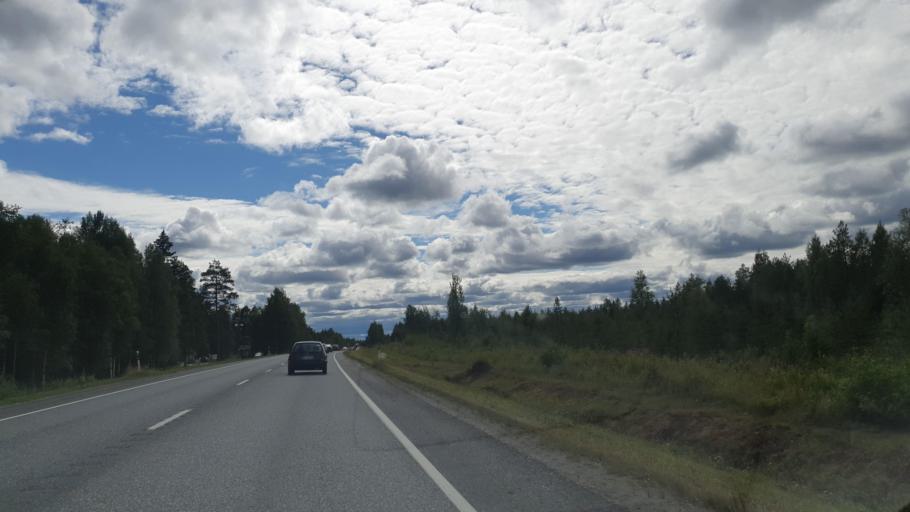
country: FI
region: Kainuu
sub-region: Kajaani
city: Kajaani
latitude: 64.1606
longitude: 27.5224
